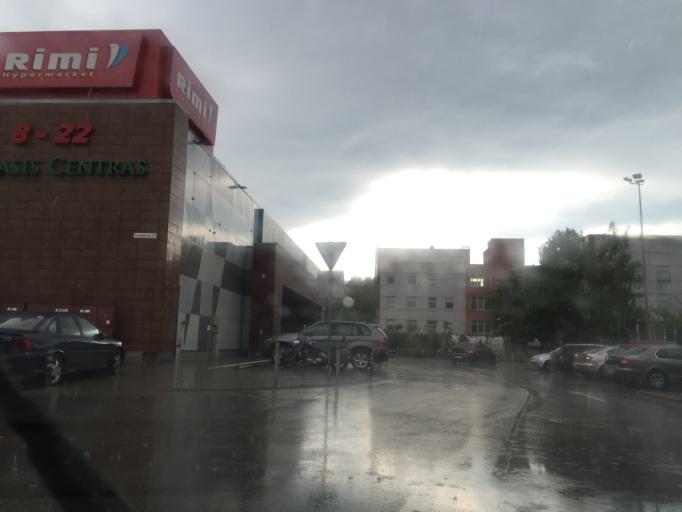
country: LT
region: Klaipedos apskritis
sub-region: Klaipeda
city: Klaipeda
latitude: 55.7520
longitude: 21.1305
